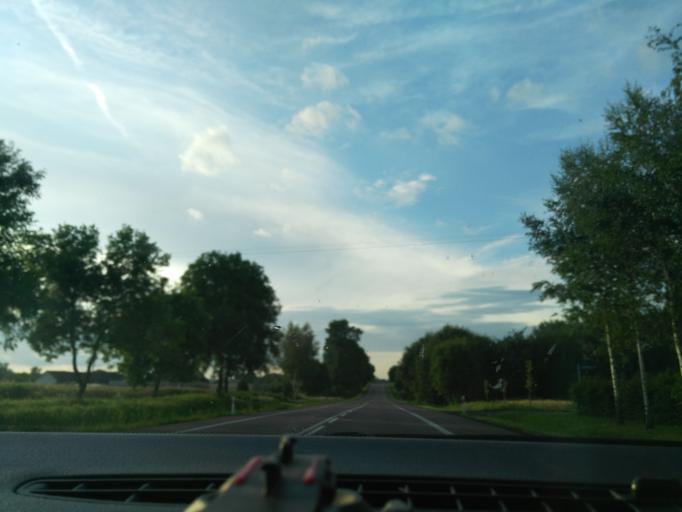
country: PL
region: Lublin Voivodeship
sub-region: Powiat lubelski
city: Niedrzwica Duza
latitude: 51.0698
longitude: 22.3784
